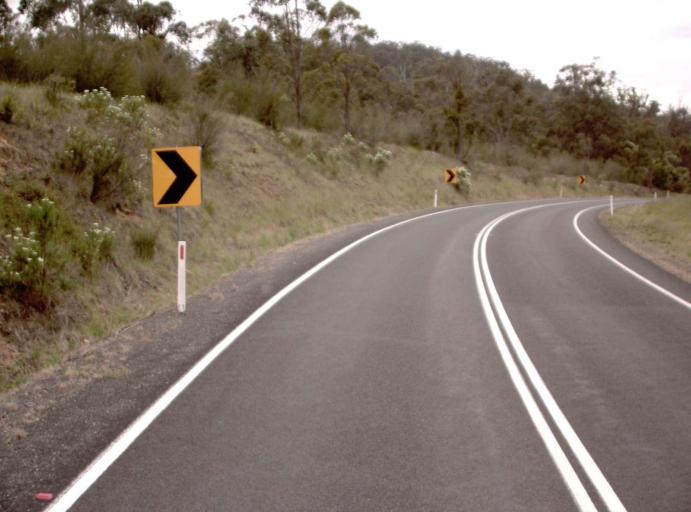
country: AU
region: New South Wales
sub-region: Bombala
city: Bombala
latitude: -37.2410
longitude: 149.2602
